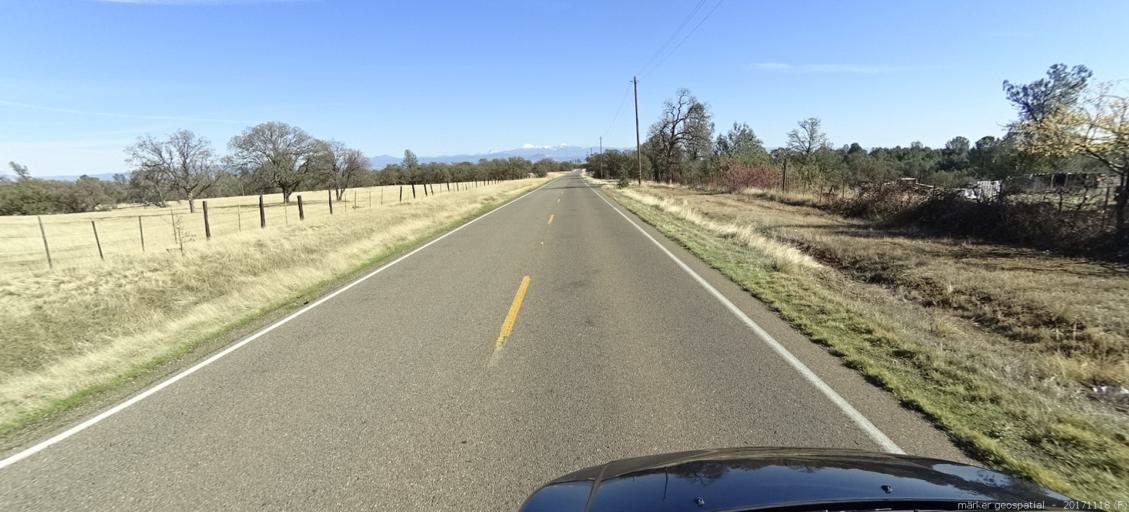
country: US
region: California
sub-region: Shasta County
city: Anderson
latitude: 40.4412
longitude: -122.3568
